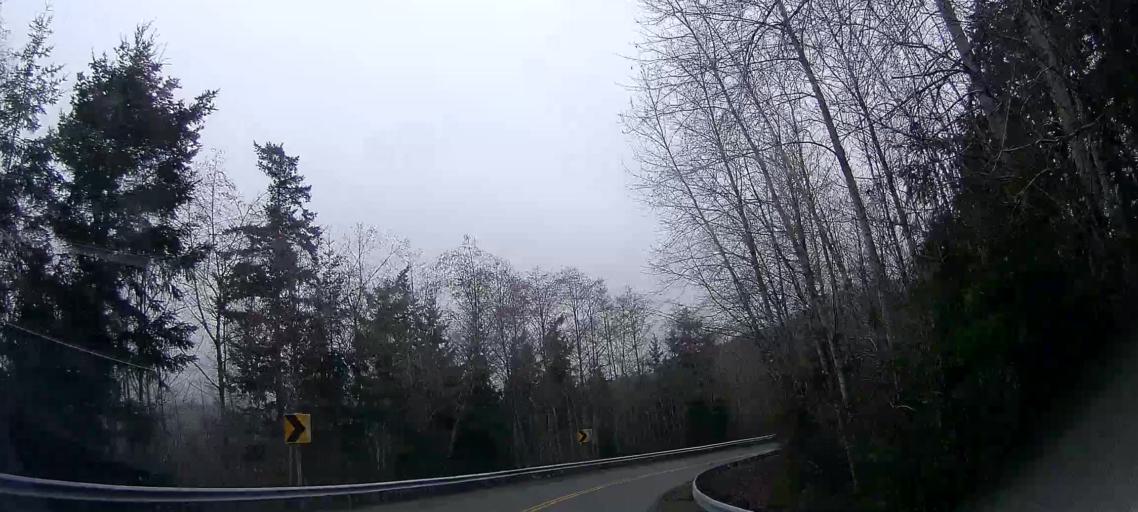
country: US
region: Washington
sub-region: Skagit County
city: Mount Vernon
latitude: 48.3758
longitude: -122.3012
